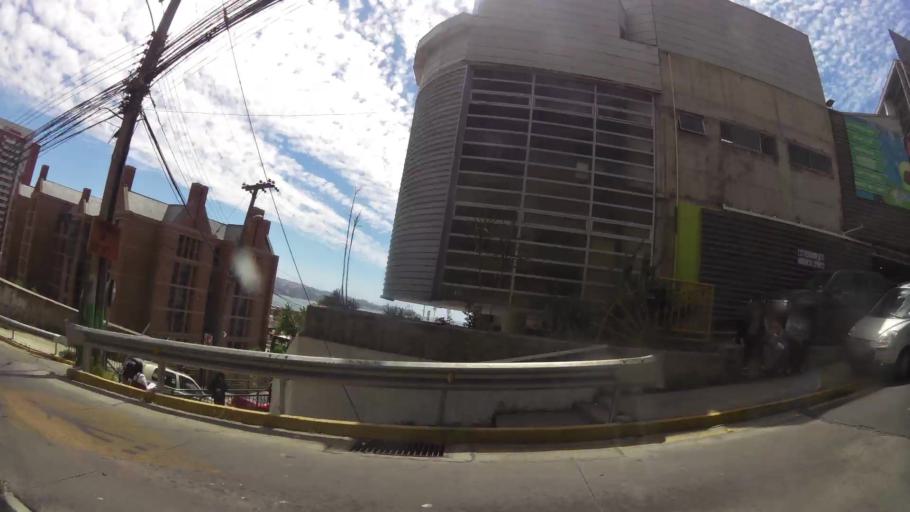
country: CL
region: Valparaiso
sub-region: Provincia de Valparaiso
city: Vina del Mar
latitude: -33.0324
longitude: -71.5882
